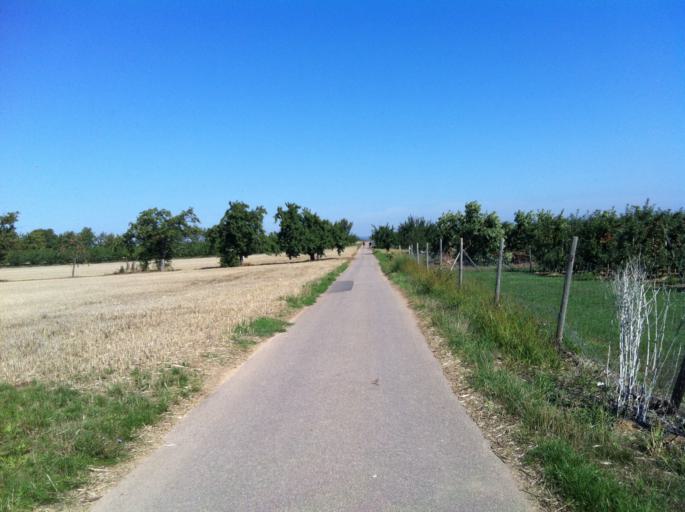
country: DE
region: Rheinland-Pfalz
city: Ober-Olm
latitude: 49.9719
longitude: 8.1771
